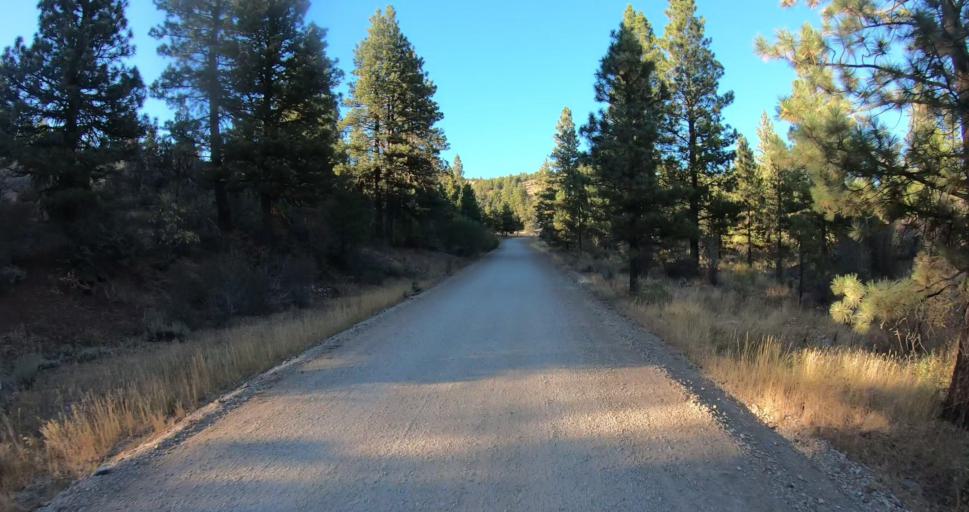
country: US
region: Oregon
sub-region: Lake County
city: Lakeview
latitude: 42.2032
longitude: -120.3006
